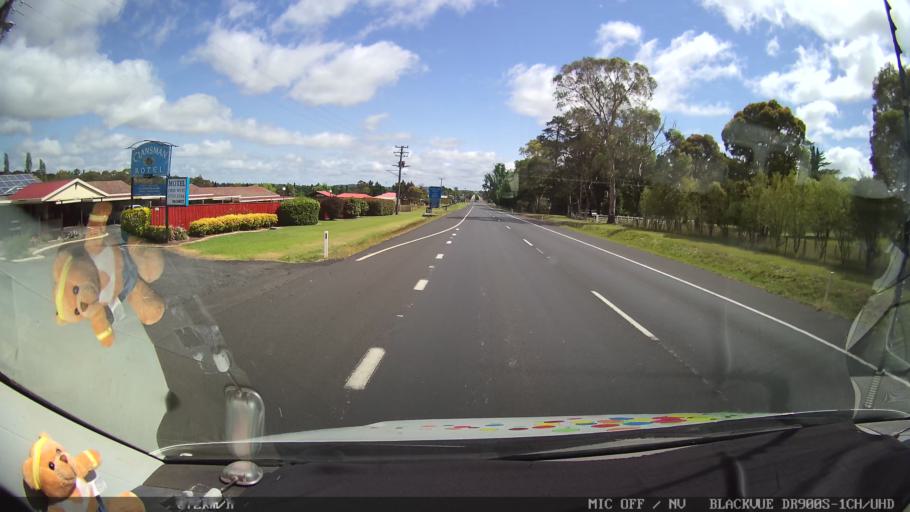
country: AU
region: New South Wales
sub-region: Glen Innes Severn
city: Glen Innes
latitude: -29.7563
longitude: 151.7347
